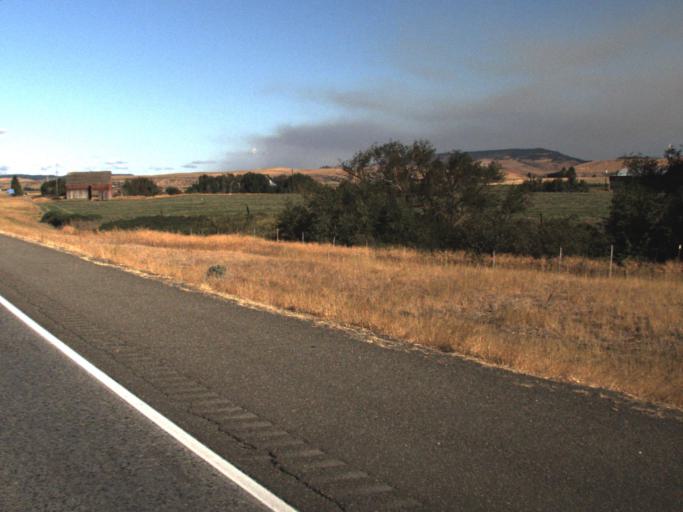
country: US
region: Washington
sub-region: Kittitas County
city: Ellensburg
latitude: 47.0628
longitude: -120.6910
